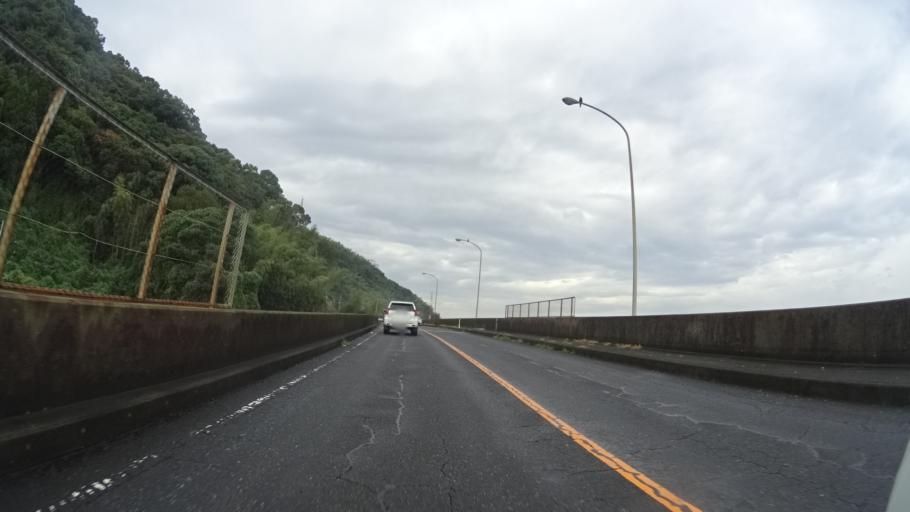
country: JP
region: Kagoshima
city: Kajiki
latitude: 31.6984
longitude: 130.6133
